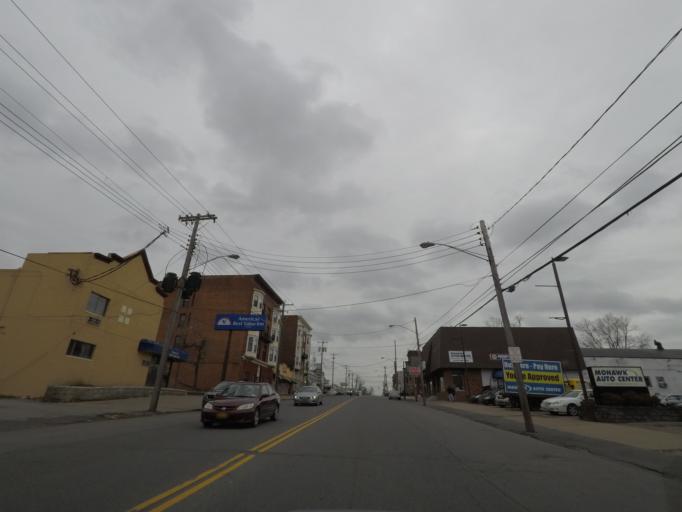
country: US
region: New York
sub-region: Schenectady County
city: Schenectady
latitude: 42.8091
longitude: -73.9366
